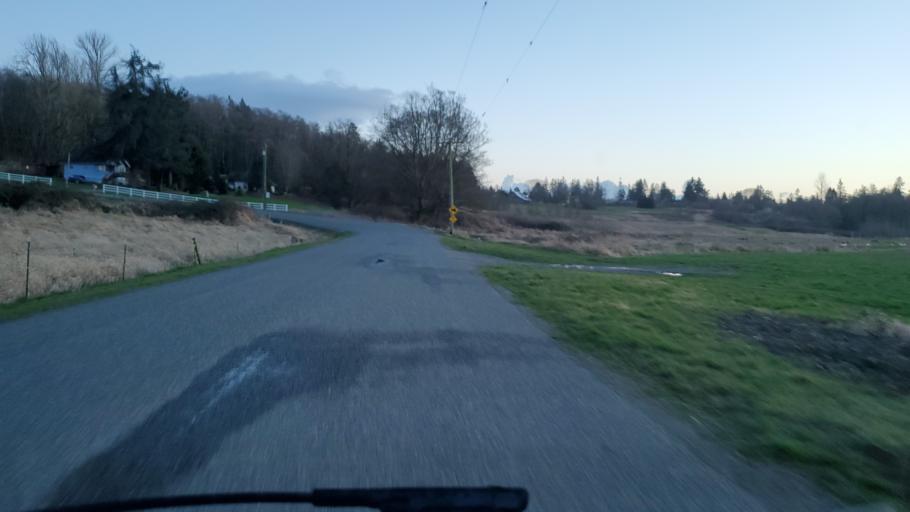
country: US
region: Washington
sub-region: Skagit County
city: Burlington
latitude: 48.4612
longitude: -122.2975
